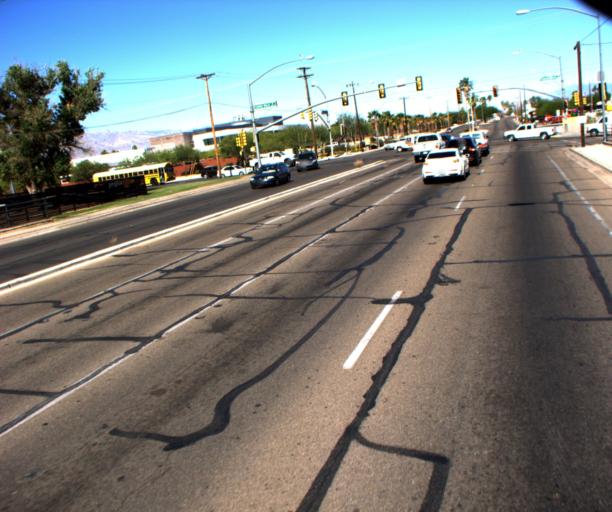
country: US
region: Arizona
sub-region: Pima County
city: Flowing Wells
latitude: 32.2611
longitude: -110.9958
